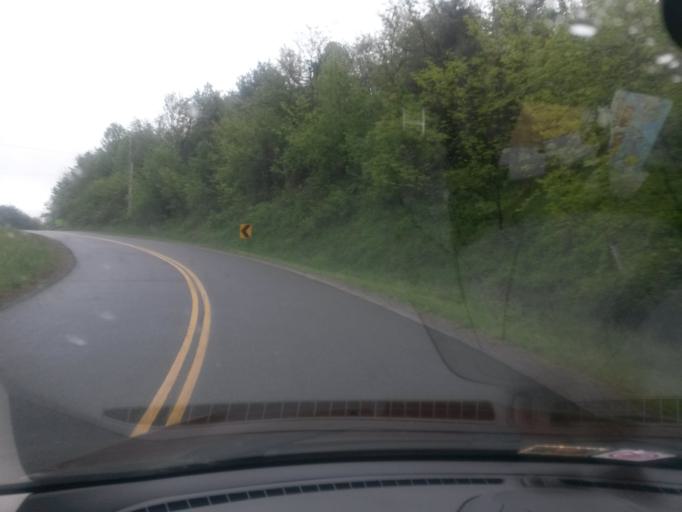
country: US
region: Virginia
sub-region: Floyd County
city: Floyd
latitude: 36.7895
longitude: -80.3878
